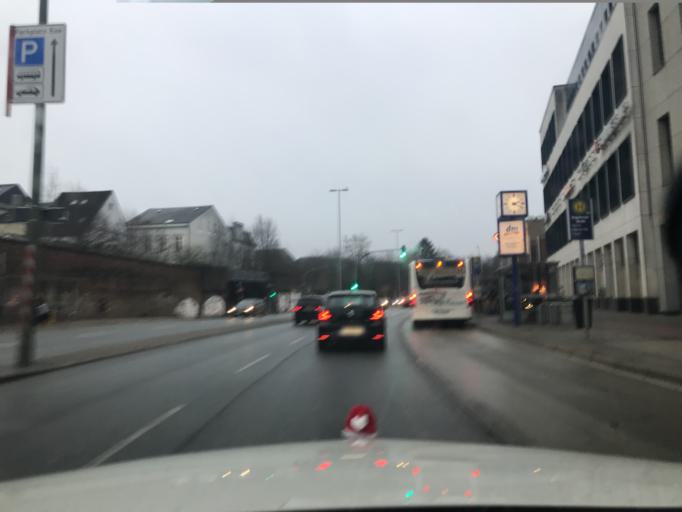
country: DE
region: Schleswig-Holstein
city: Flensburg
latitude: 54.7835
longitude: 9.4392
